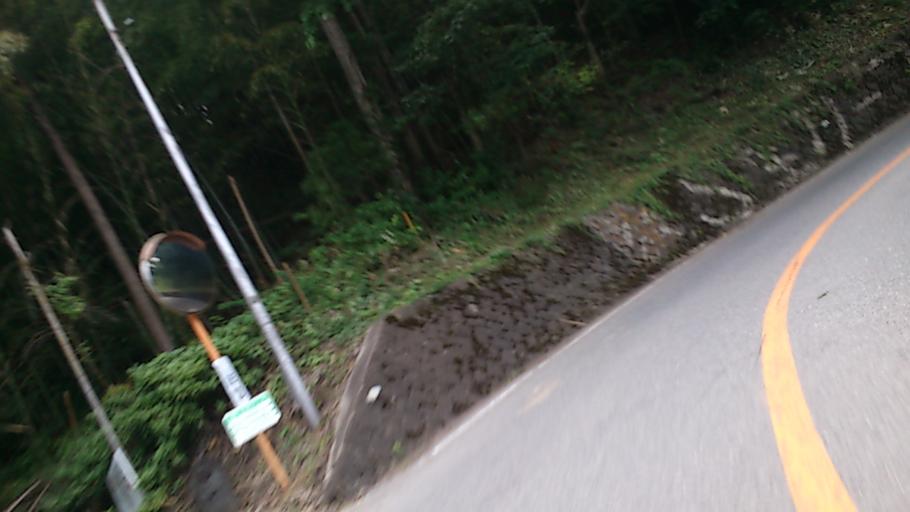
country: JP
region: Yamagata
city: Kaminoyama
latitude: 38.1422
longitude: 140.3389
